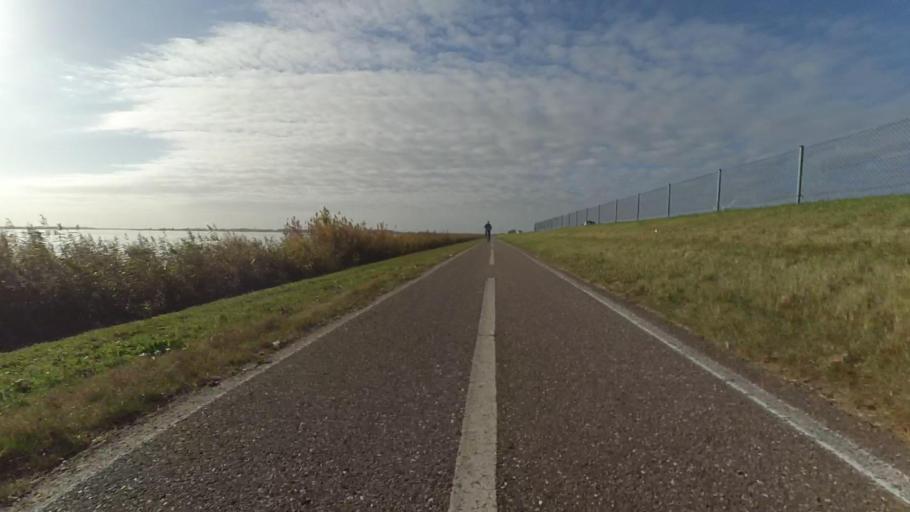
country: NL
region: Flevoland
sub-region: Gemeente Zeewolde
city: Zeewolde
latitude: 52.3584
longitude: 5.5500
